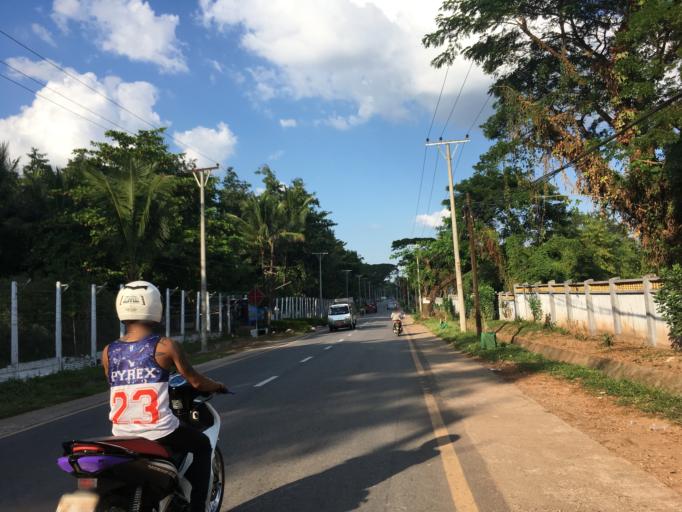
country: MM
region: Mon
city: Mawlamyine
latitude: 16.4400
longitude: 97.6162
